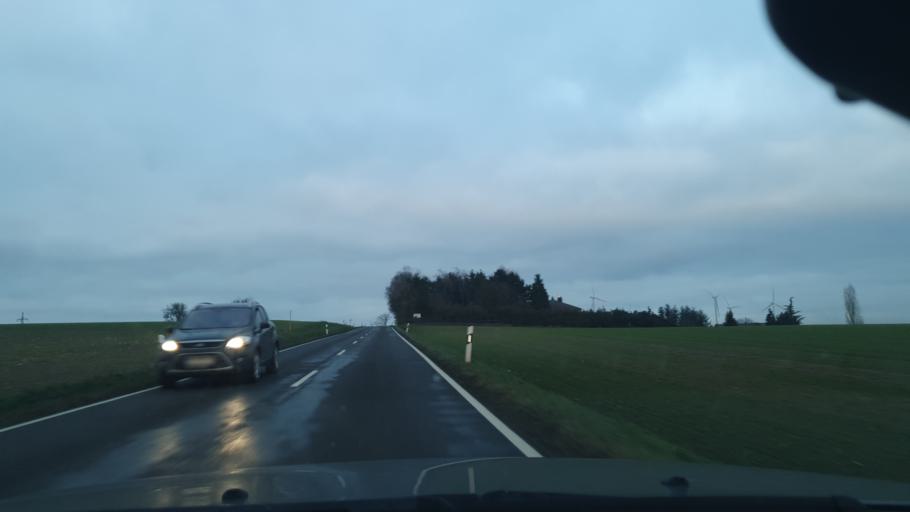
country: DE
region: Rheinland-Pfalz
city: Rosenkopf
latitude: 49.3424
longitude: 7.4297
